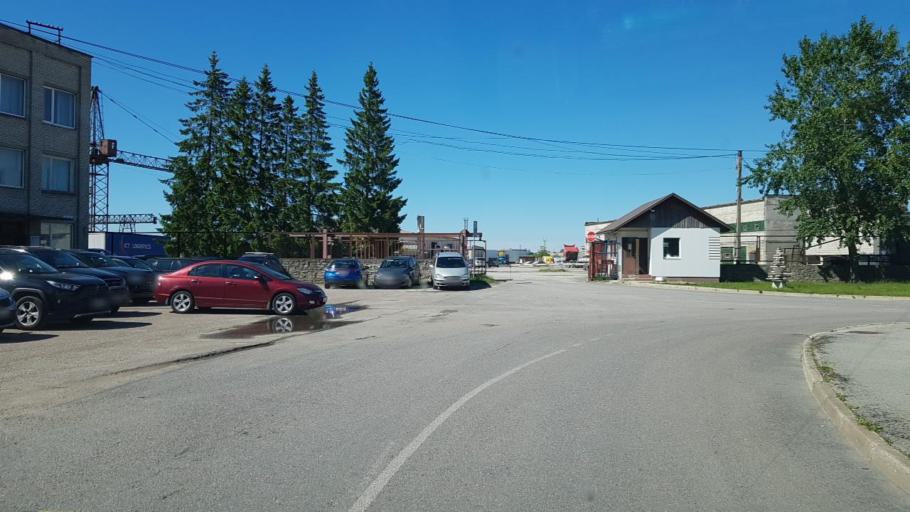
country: EE
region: Ida-Virumaa
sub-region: Narva linn
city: Narva
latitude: 59.3593
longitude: 28.1748
